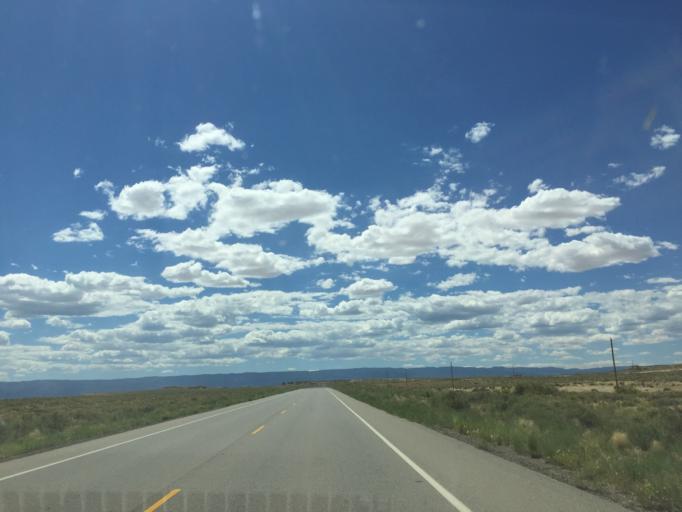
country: US
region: New Mexico
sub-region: San Juan County
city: Waterflow
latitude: 36.3515
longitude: -108.6271
